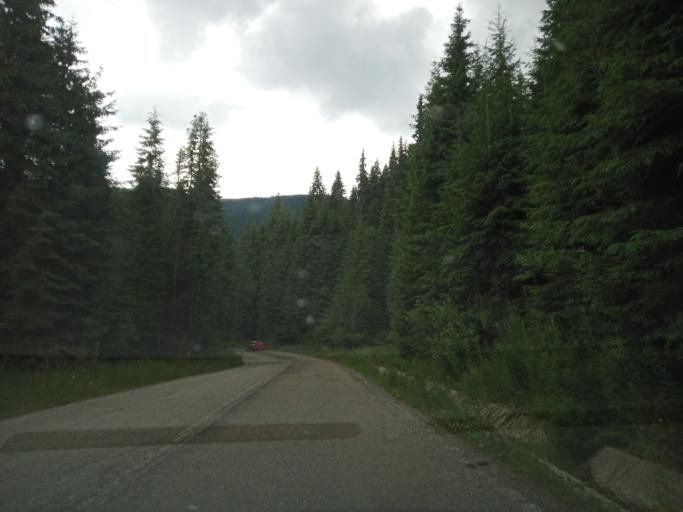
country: RO
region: Valcea
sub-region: Comuna Voineasa
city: Voineasa
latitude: 45.4149
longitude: 23.7240
